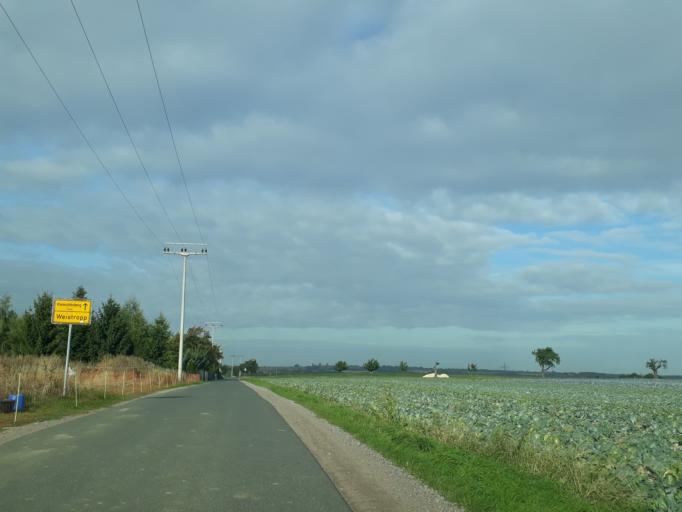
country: DE
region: Saxony
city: Klipphausen
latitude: 51.0843
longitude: 13.5808
